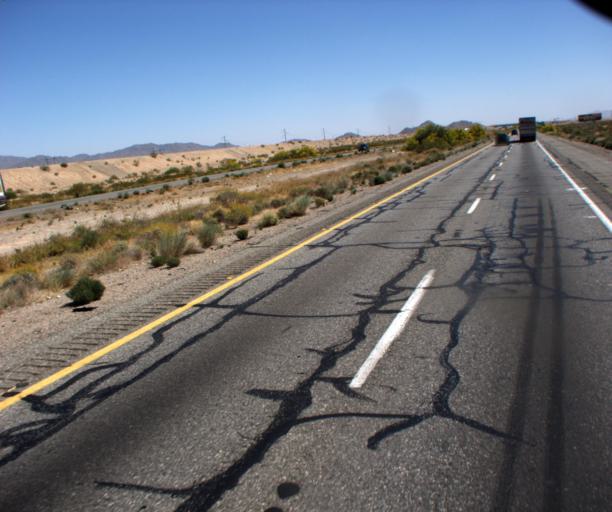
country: US
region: Arizona
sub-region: Maricopa County
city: Buckeye
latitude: 33.4422
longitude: -112.6911
